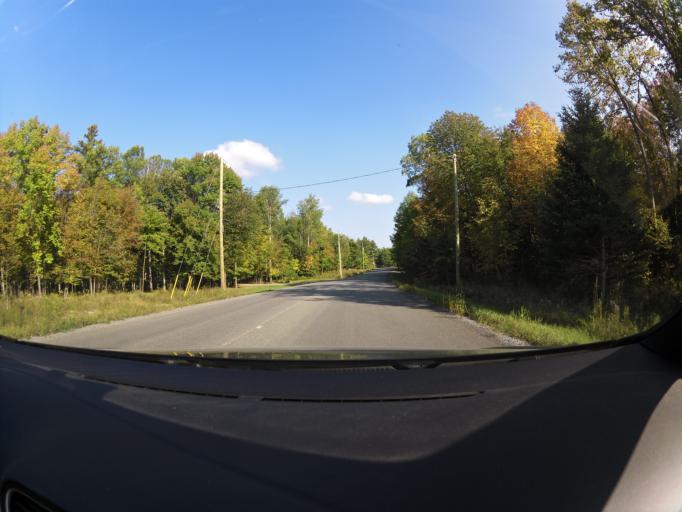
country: CA
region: Ontario
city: Arnprior
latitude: 45.4445
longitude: -76.2658
